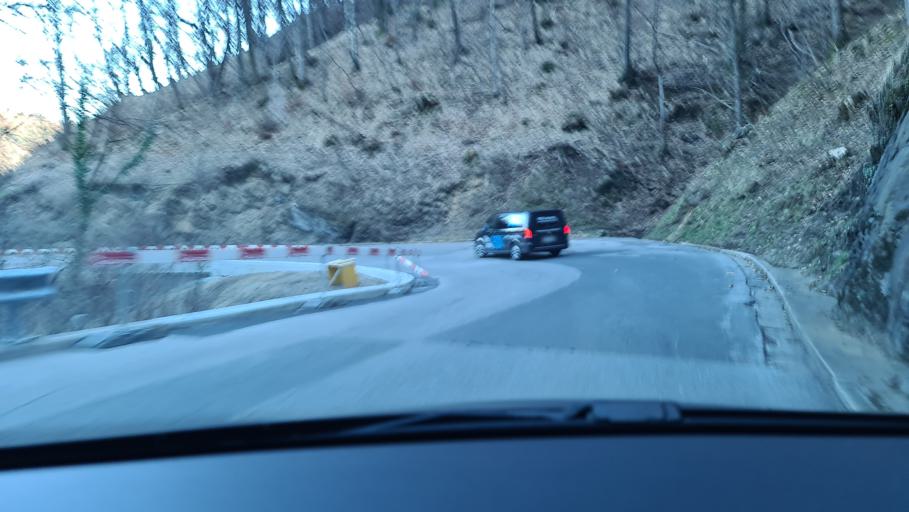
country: CH
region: Ticino
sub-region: Lugano District
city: Pura
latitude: 46.0283
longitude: 8.8551
